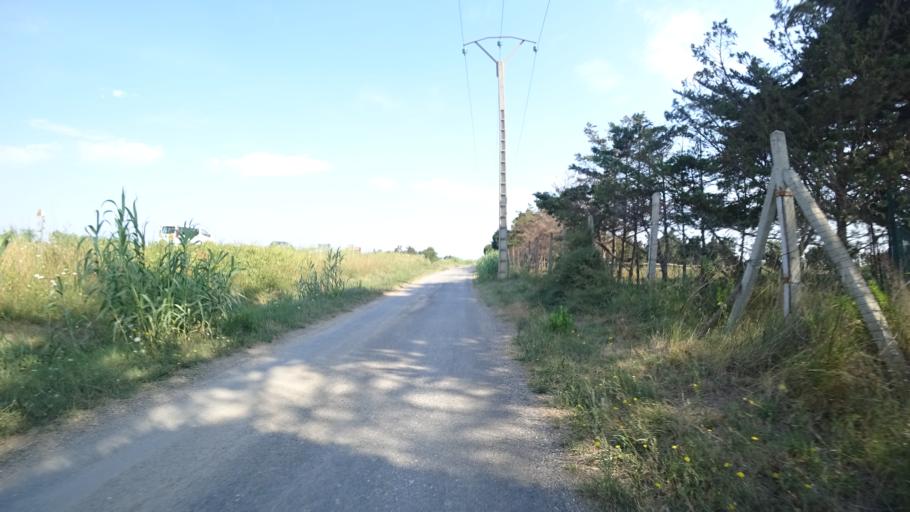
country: FR
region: Languedoc-Roussillon
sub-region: Departement des Pyrenees-Orientales
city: Le Barcares
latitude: 42.7760
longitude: 3.0165
